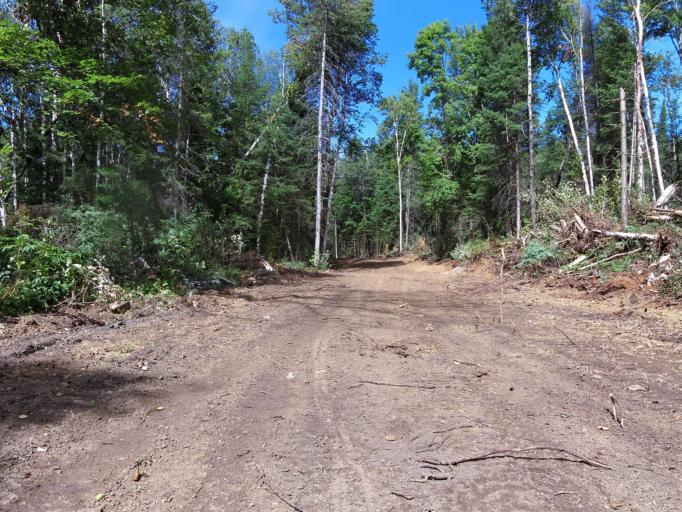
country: CA
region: Ontario
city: Renfrew
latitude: 45.1047
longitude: -76.7145
